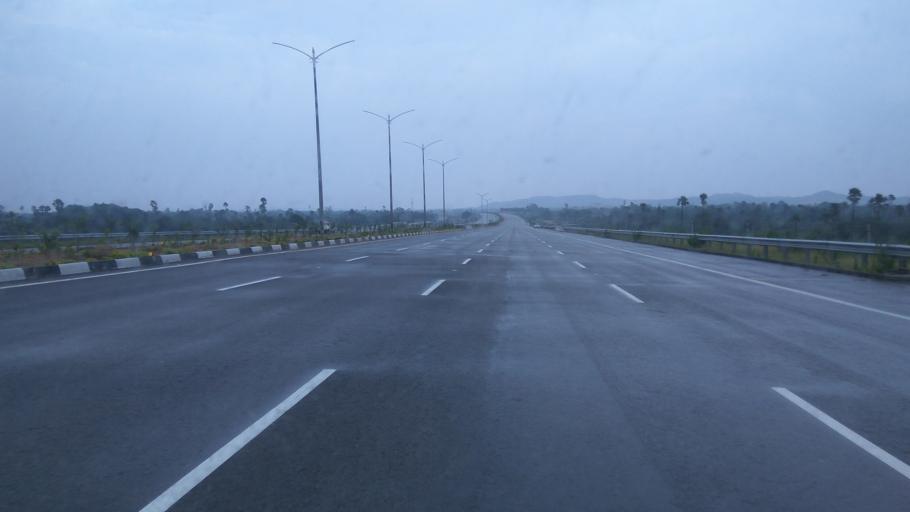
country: IN
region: Telangana
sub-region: Rangareddi
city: Ghatkesar
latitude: 17.4551
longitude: 78.6692
